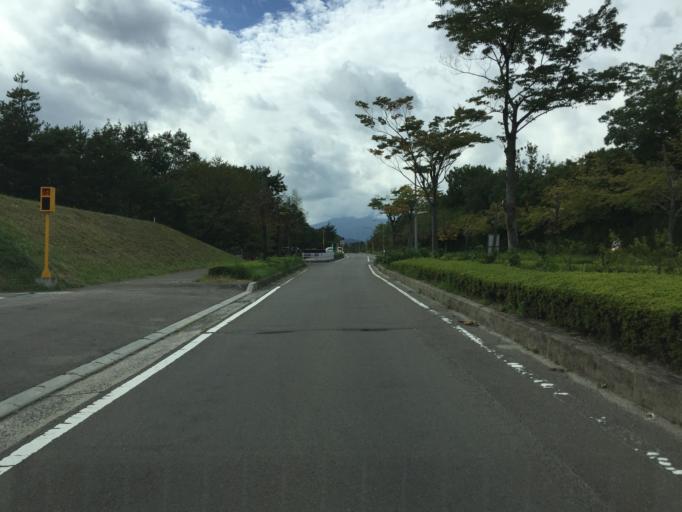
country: JP
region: Fukushima
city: Fukushima-shi
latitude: 37.6882
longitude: 140.4713
